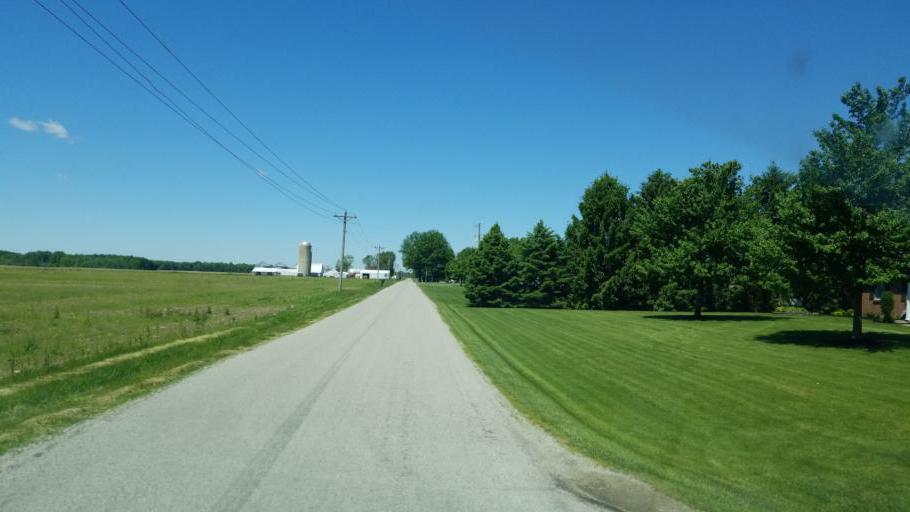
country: US
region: Ohio
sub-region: Shelby County
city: Anna
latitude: 40.3726
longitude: -84.2594
